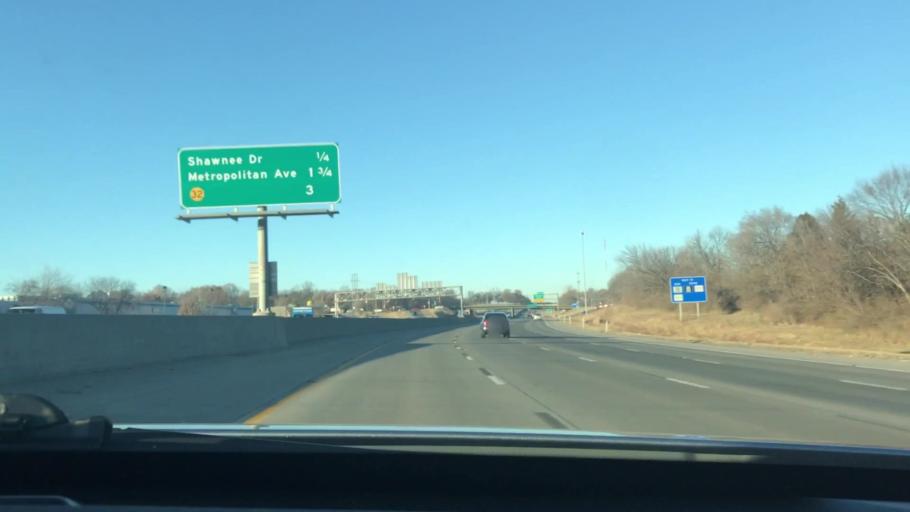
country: US
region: Kansas
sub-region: Johnson County
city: Merriam
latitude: 39.0483
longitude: -94.6788
